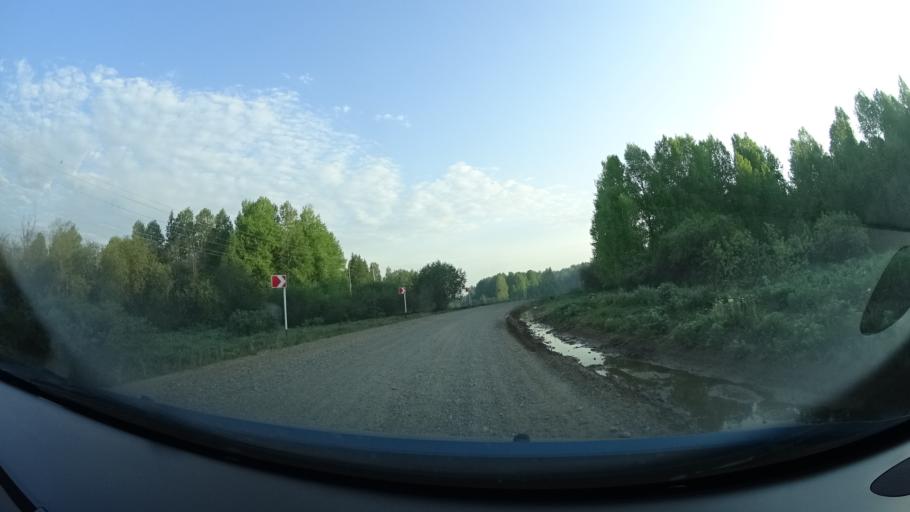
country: RU
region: Perm
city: Barda
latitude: 56.7077
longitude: 55.6767
